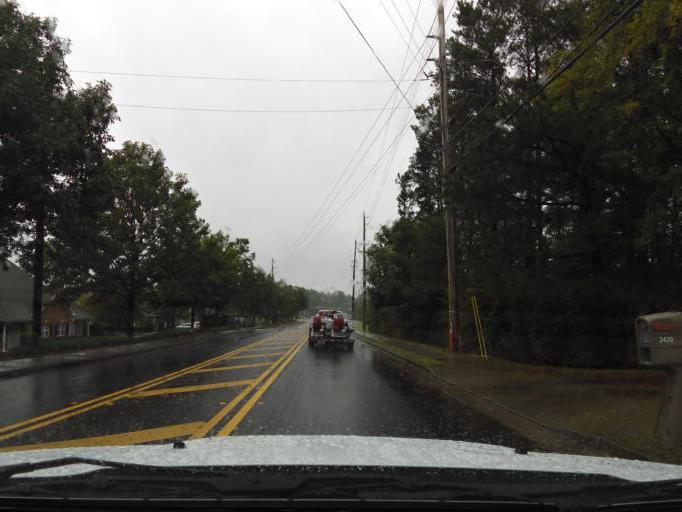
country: US
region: Georgia
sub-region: Cobb County
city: Acworth
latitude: 34.0361
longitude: -84.6752
